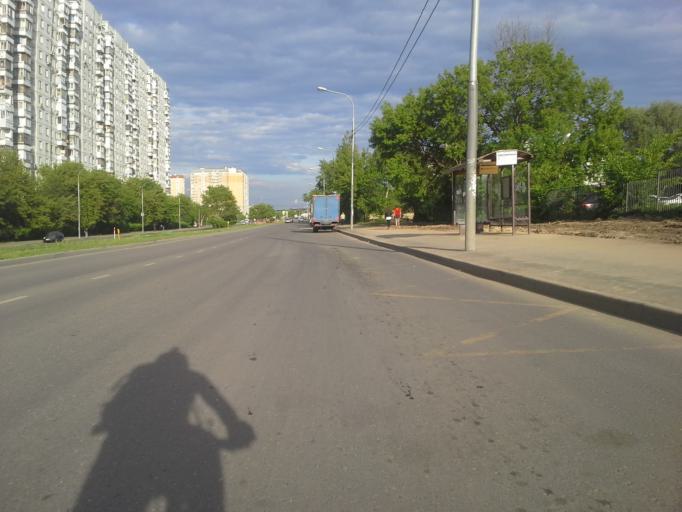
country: RU
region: Moscow
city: Solntsevo
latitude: 55.6443
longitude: 37.3992
